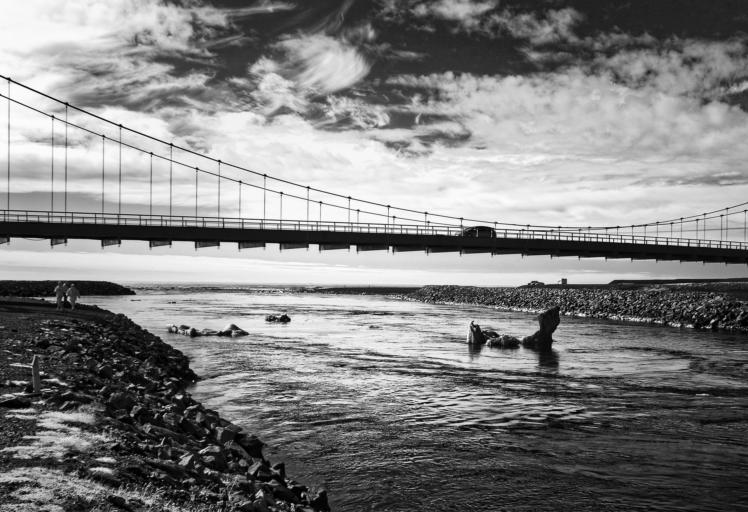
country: IS
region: East
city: Hoefn
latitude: 64.0464
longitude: -16.1797
